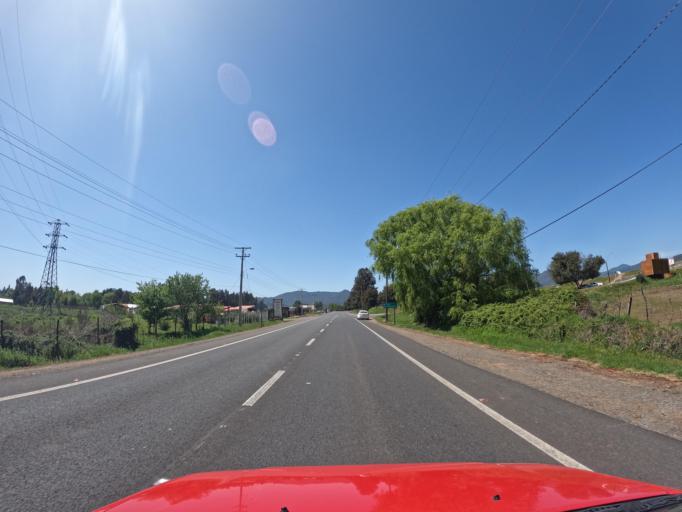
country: CL
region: Maule
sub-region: Provincia de Linares
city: Colbun
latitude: -35.7154
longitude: -71.4048
